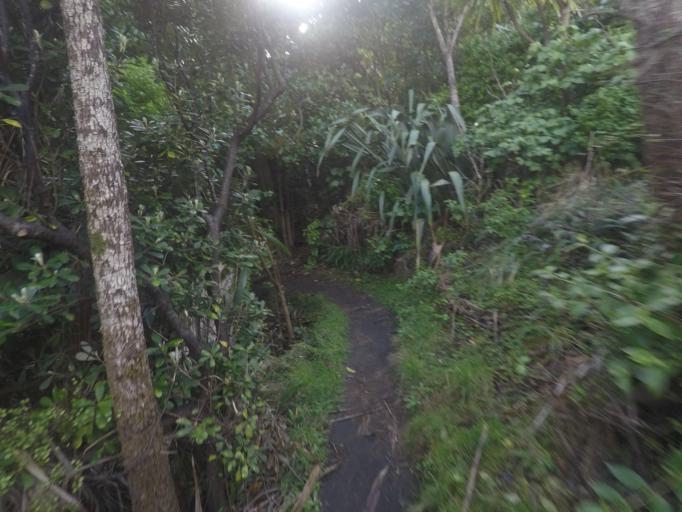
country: NZ
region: Auckland
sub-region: Auckland
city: Muriwai Beach
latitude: -36.8821
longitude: 174.4402
